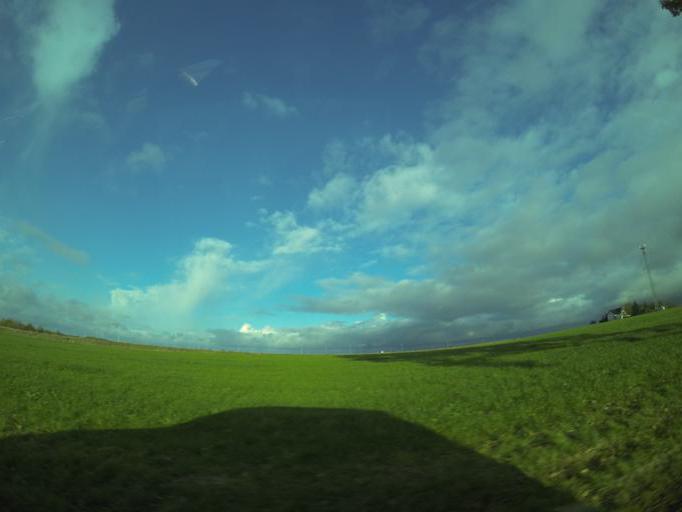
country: DE
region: Thuringia
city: Vollmershain
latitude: 50.8586
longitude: 12.3046
